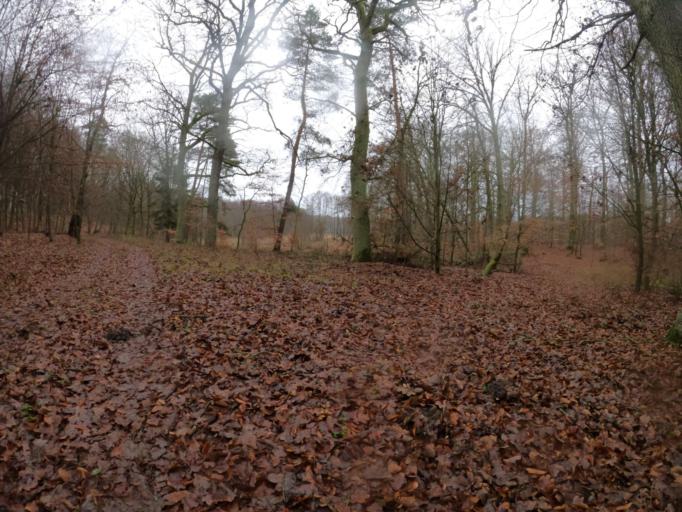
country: PL
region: West Pomeranian Voivodeship
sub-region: Powiat mysliborski
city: Debno
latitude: 52.7536
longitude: 14.7682
